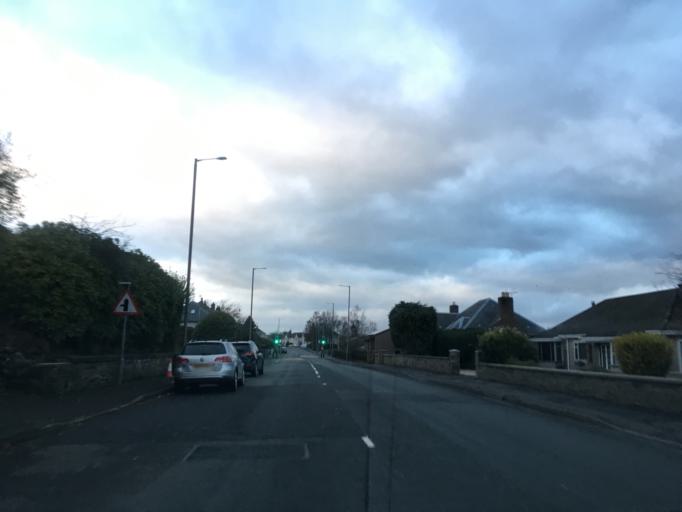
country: GB
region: Scotland
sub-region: Stirling
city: Bannockburn
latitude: 56.0975
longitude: -3.9269
